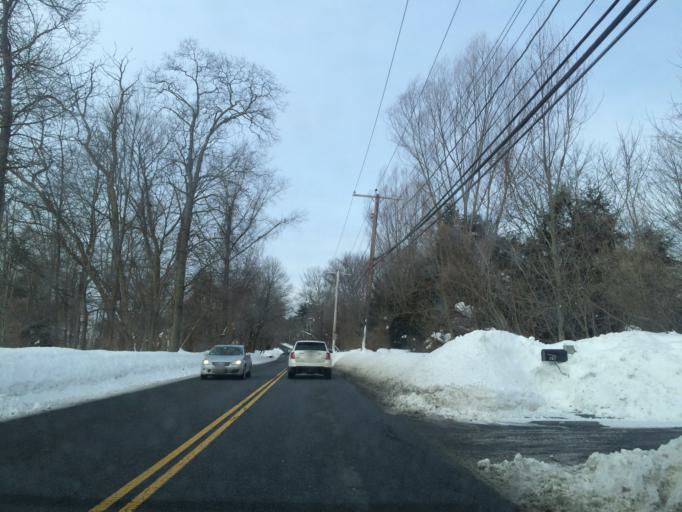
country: US
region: Massachusetts
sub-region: Middlesex County
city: Weston
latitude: 42.3408
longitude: -71.2761
